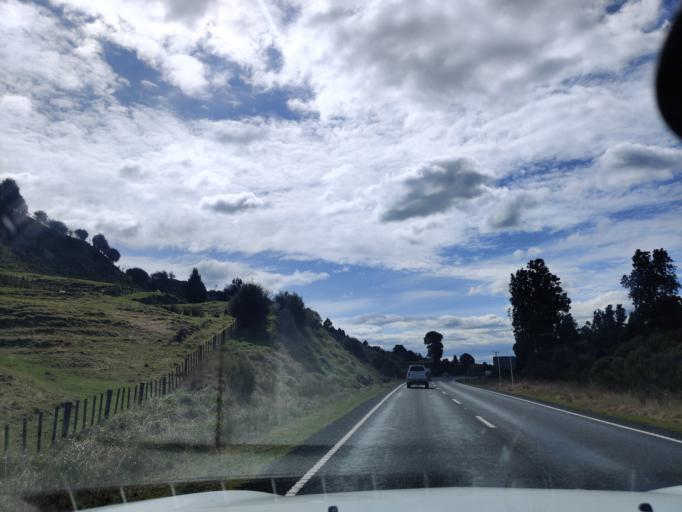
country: NZ
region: Waikato
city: Turangi
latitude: -39.1213
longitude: 175.3901
